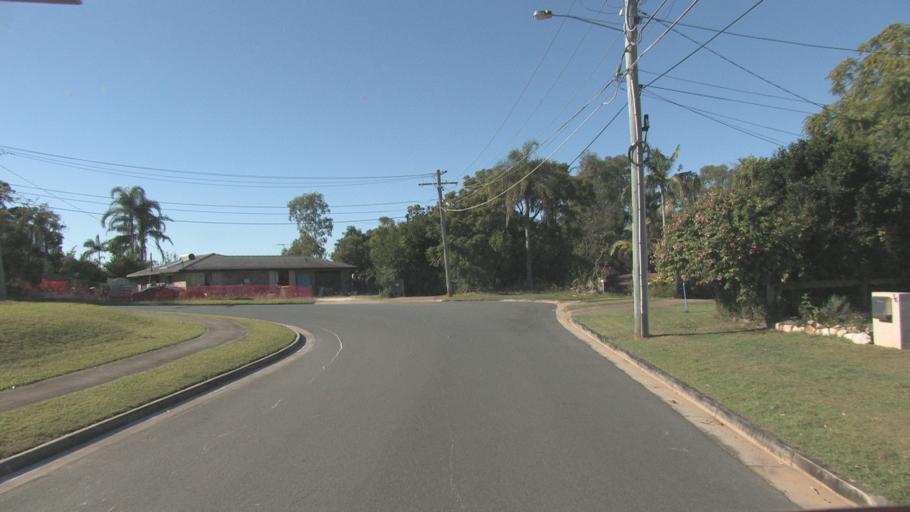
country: AU
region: Queensland
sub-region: Logan
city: Slacks Creek
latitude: -27.6453
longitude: 153.1426
